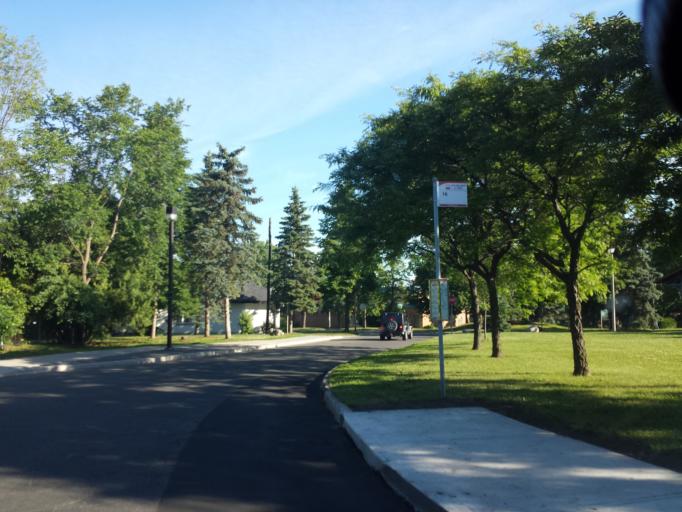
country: CA
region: Ontario
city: Bells Corners
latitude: 45.3628
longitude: -75.8009
